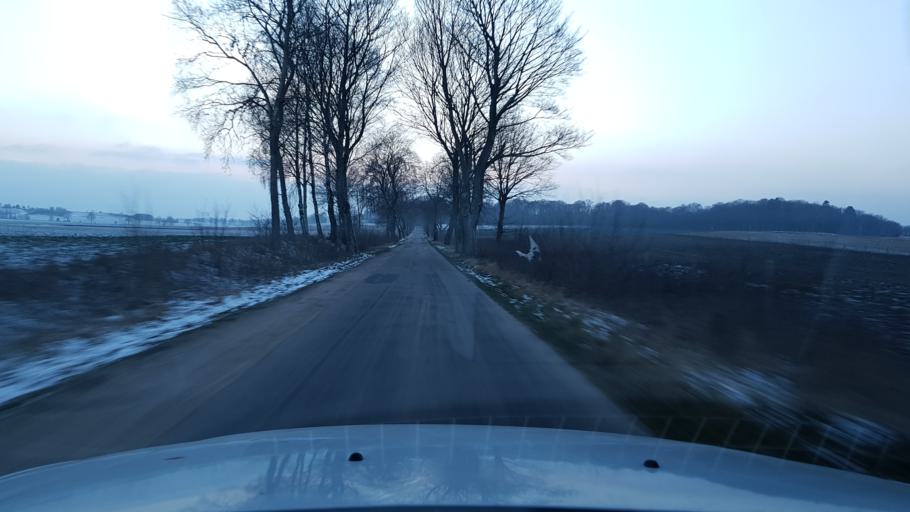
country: PL
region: West Pomeranian Voivodeship
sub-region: Powiat swidwinski
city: Slawoborze
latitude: 53.9740
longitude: 15.7778
